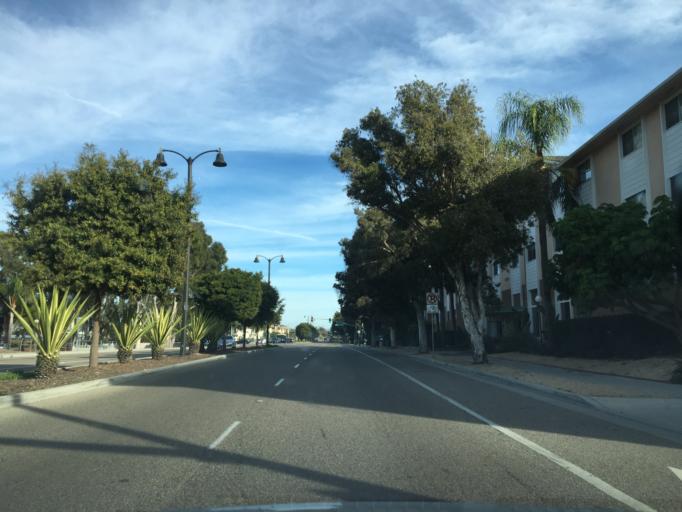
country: US
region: California
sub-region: Santa Barbara County
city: Isla Vista
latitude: 34.4173
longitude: -119.8625
